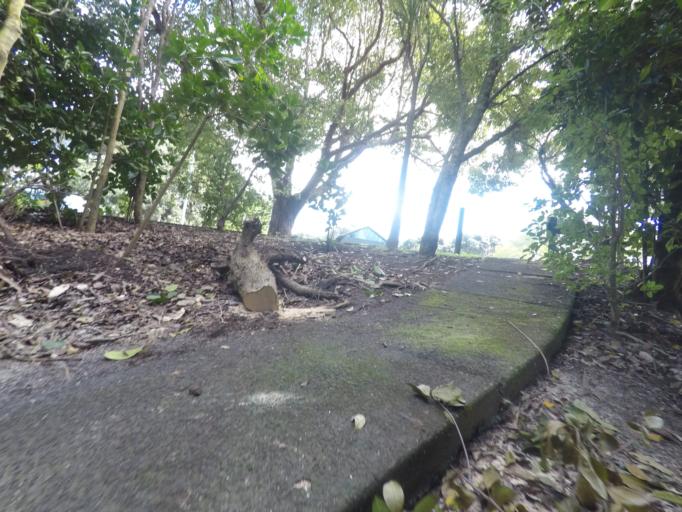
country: NZ
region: Auckland
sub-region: Auckland
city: Auckland
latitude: -36.8570
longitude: 174.7183
